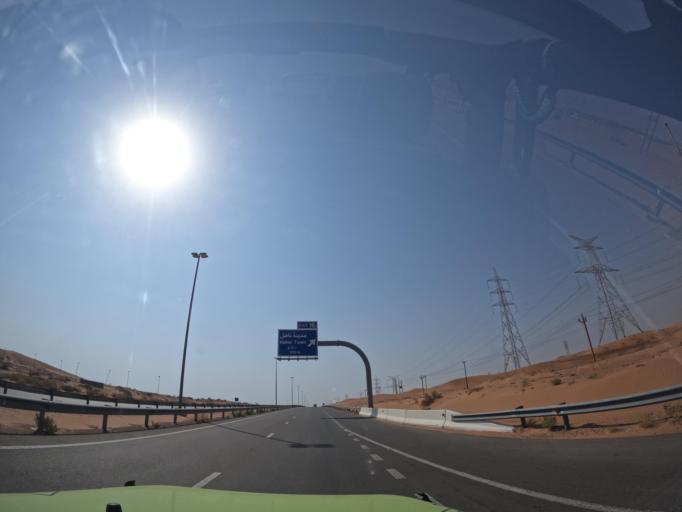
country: OM
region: Al Buraimi
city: Al Buraymi
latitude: 24.3491
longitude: 55.7377
